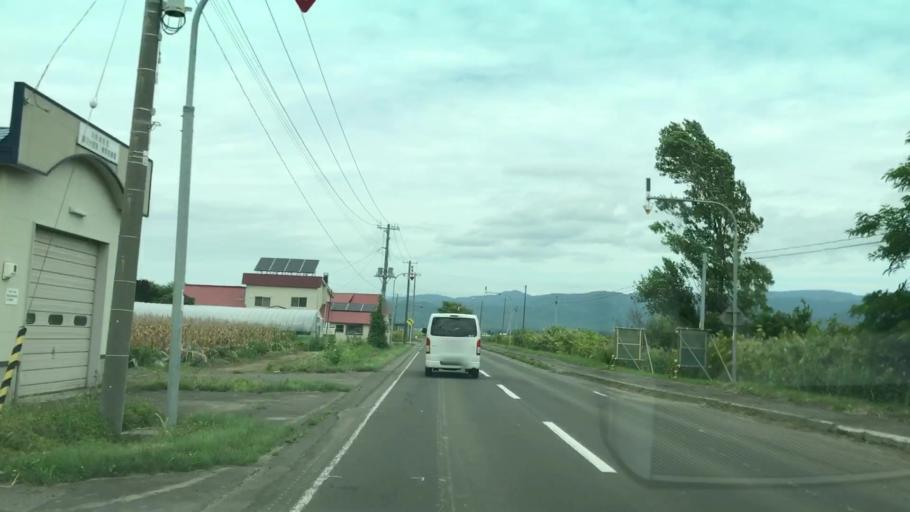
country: JP
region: Hokkaido
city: Iwanai
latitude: 43.0030
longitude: 140.5853
